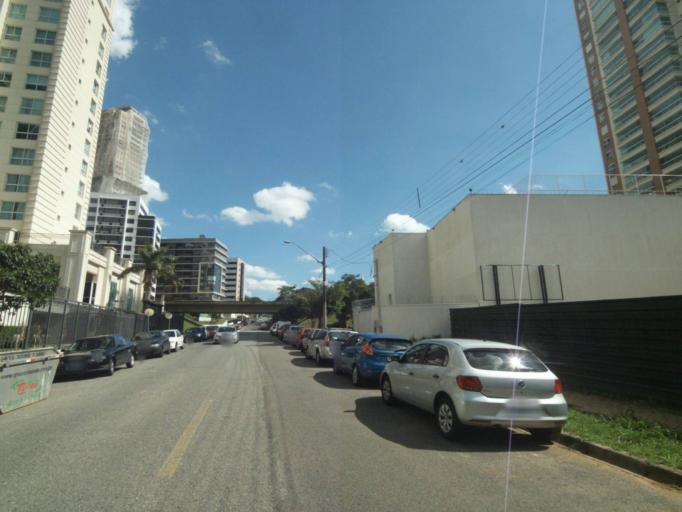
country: BR
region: Parana
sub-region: Curitiba
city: Curitiba
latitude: -25.4398
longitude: -49.3403
